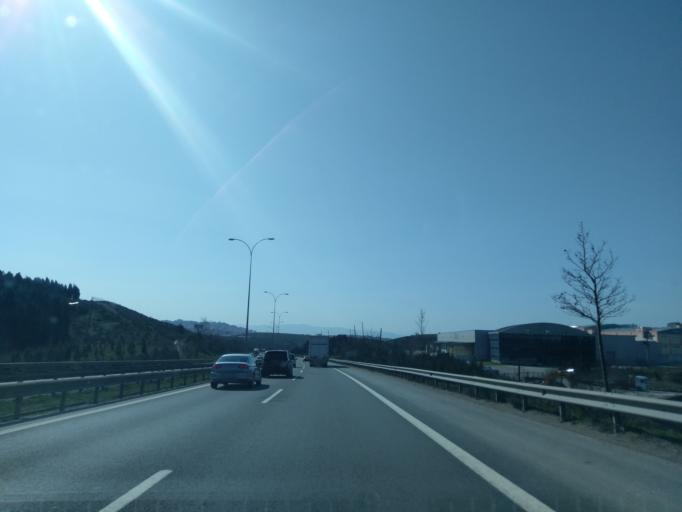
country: TR
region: Kocaeli
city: Balcik
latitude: 40.8515
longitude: 29.3747
